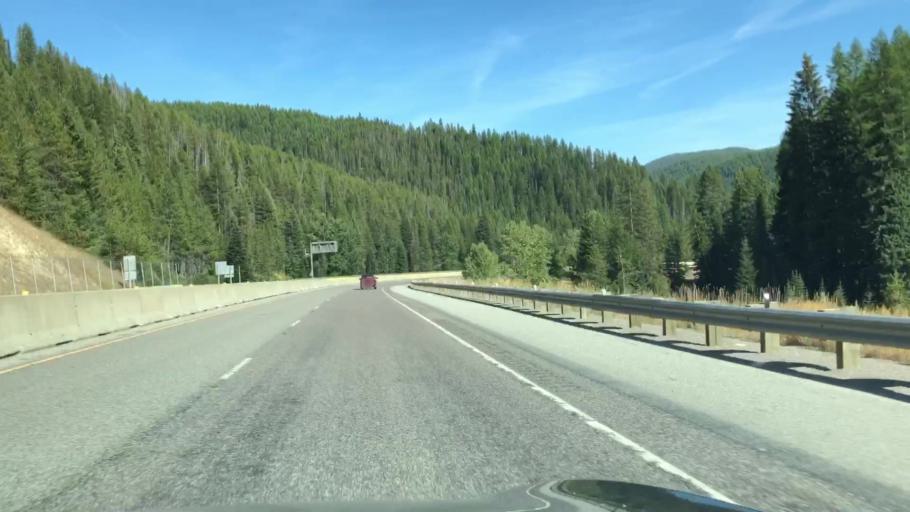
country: US
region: Montana
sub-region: Sanders County
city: Thompson Falls
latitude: 47.4187
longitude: -115.5958
